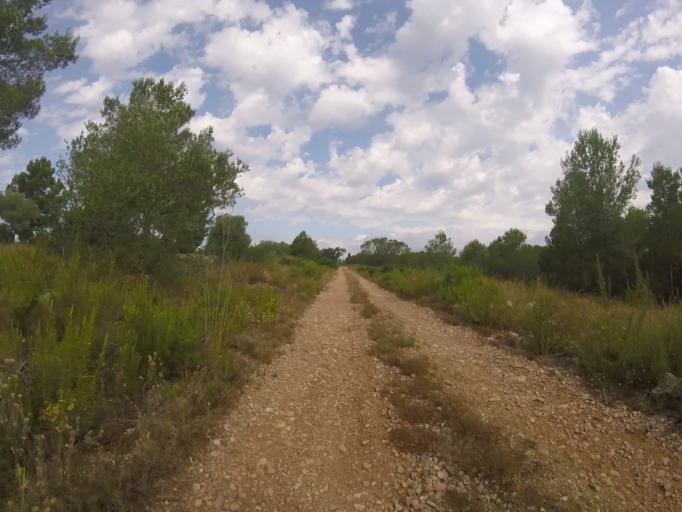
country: ES
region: Valencia
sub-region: Provincia de Castello
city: Alcala de Xivert
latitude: 40.3629
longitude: 0.1978
